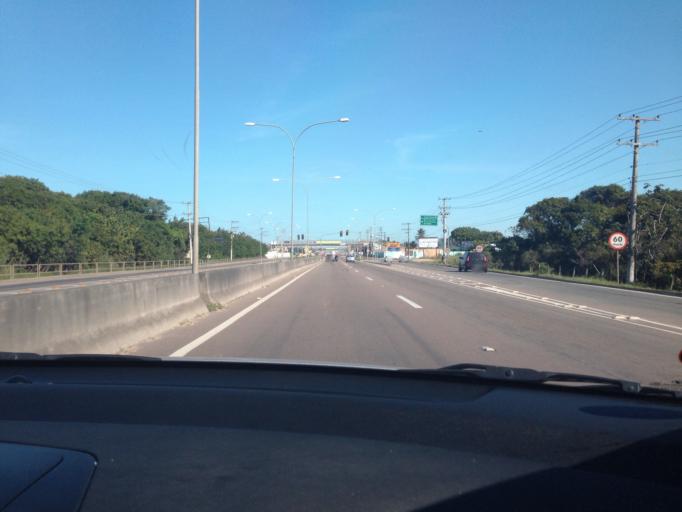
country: BR
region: Espirito Santo
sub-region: Vila Velha
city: Vila Velha
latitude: -20.4173
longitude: -40.3285
